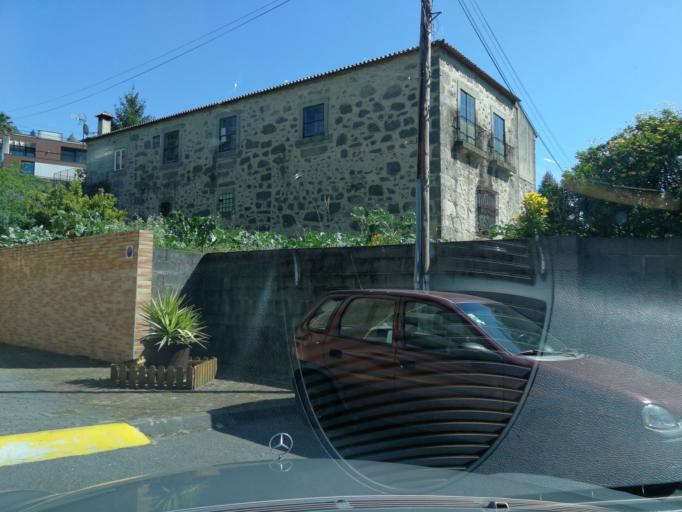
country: PT
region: Braga
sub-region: Braga
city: Adaufe
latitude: 41.5606
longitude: -8.3841
